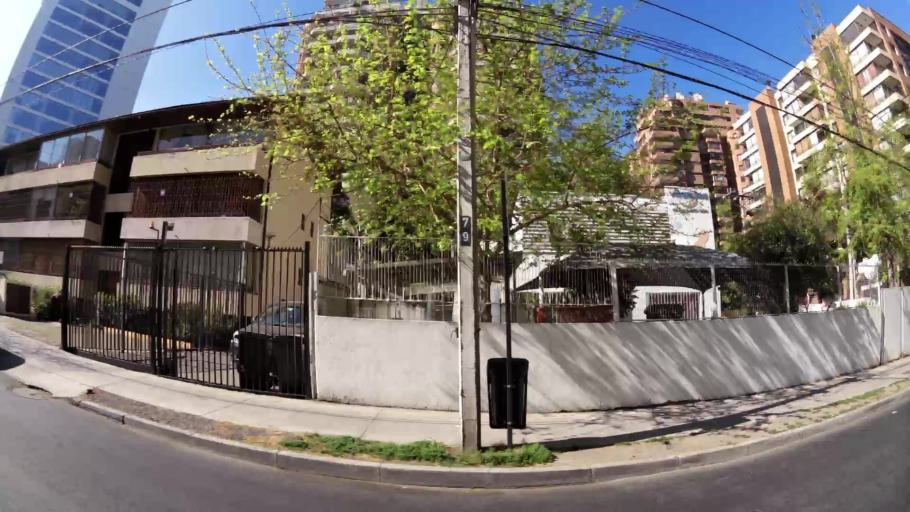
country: CL
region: Santiago Metropolitan
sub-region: Provincia de Santiago
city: Villa Presidente Frei, Nunoa, Santiago, Chile
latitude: -33.4073
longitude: -70.5742
